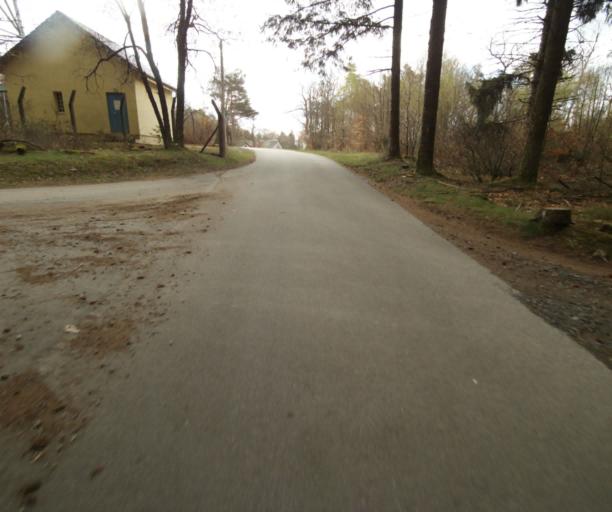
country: FR
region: Limousin
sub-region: Departement de la Correze
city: Correze
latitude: 45.3202
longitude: 1.9437
